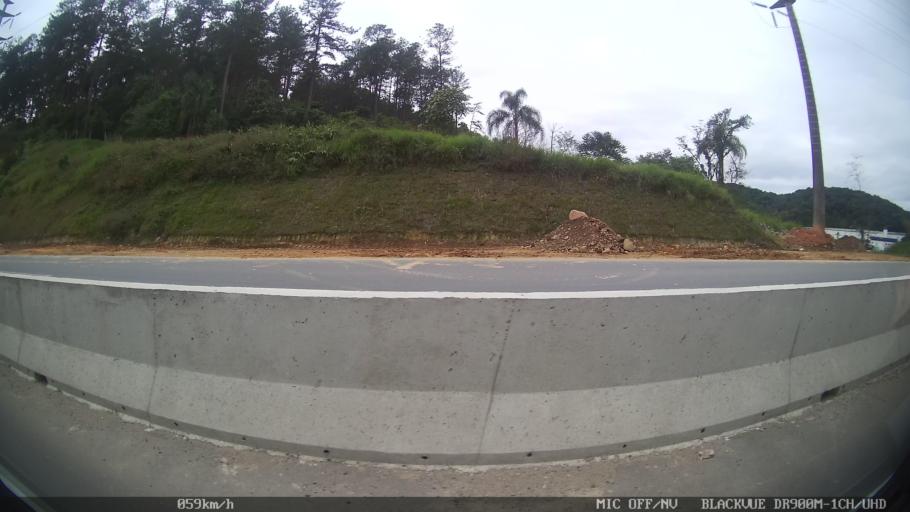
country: BR
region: Santa Catarina
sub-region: Joinville
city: Joinville
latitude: -26.2569
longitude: -48.8972
